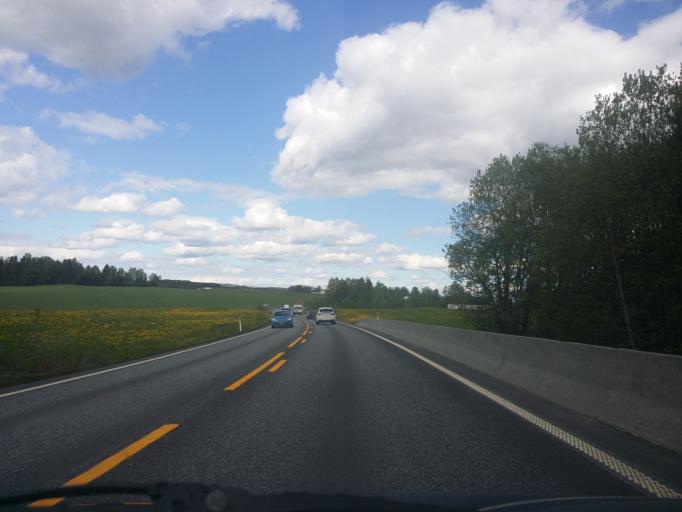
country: NO
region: Oppland
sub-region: Lunner
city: Roa
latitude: 60.2796
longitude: 10.5249
